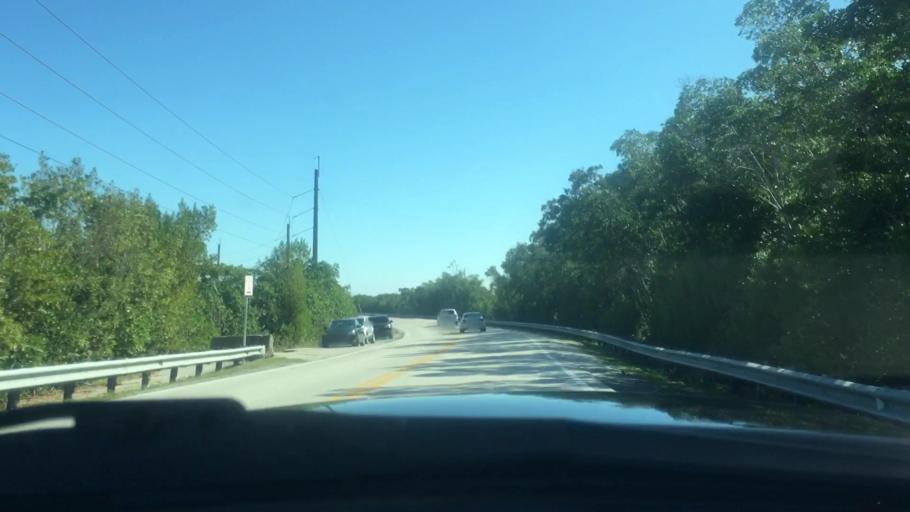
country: US
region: Florida
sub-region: Monroe County
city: North Key Largo
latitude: 25.2793
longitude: -80.3426
